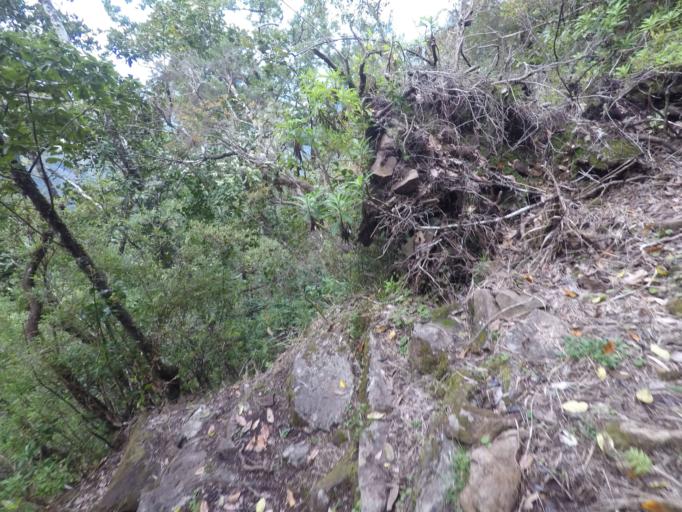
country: PT
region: Madeira
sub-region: Camara de Lobos
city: Curral das Freiras
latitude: 32.7703
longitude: -16.9776
